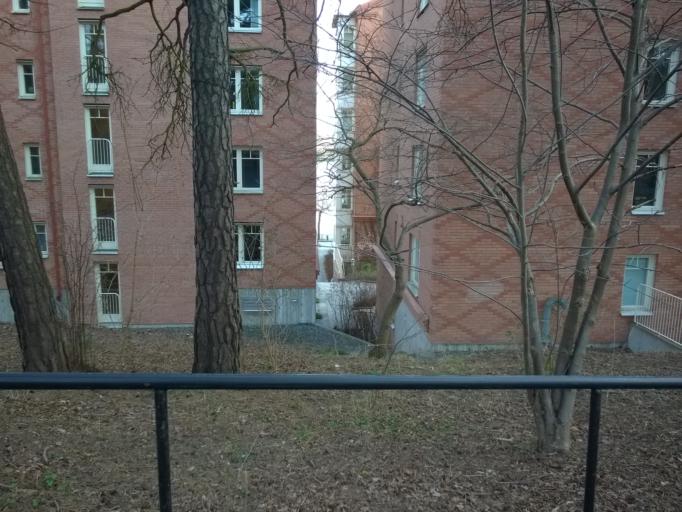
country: SE
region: Stockholm
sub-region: Solna Kommun
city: Solna
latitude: 59.3326
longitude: 17.9895
